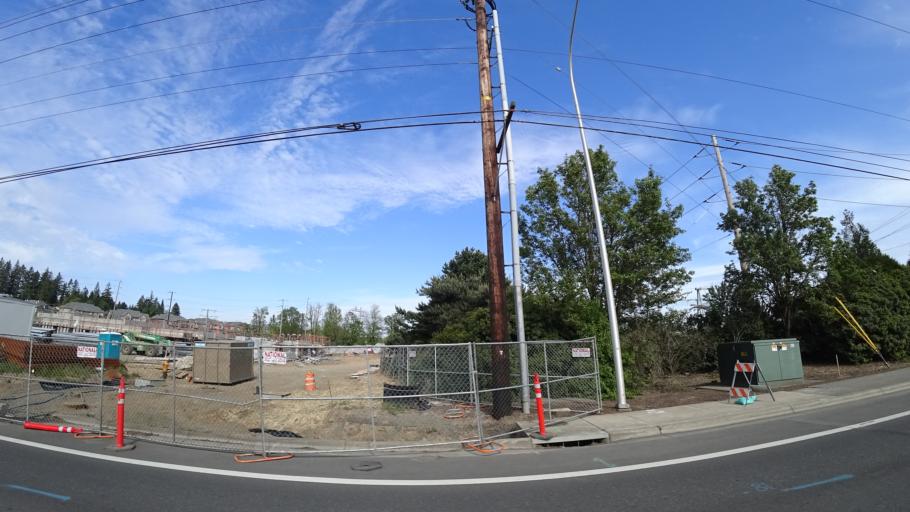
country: US
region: Oregon
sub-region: Washington County
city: Rockcreek
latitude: 45.5247
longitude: -122.8999
